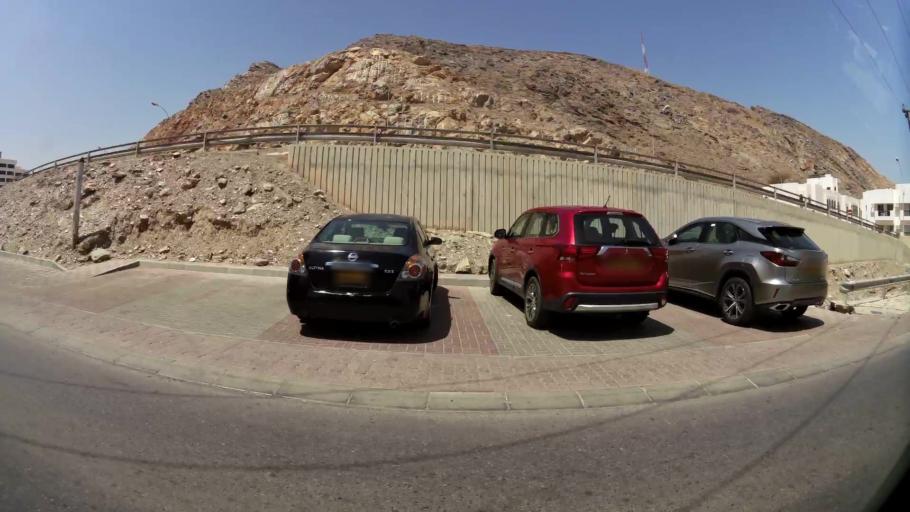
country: OM
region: Muhafazat Masqat
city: Muscat
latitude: 23.5942
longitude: 58.5417
